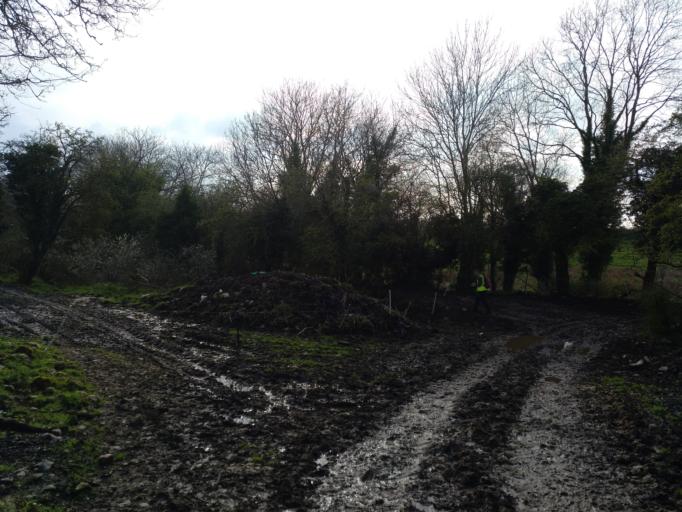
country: IE
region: Ulster
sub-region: County Monaghan
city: Clones
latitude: 54.1980
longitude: -7.1383
